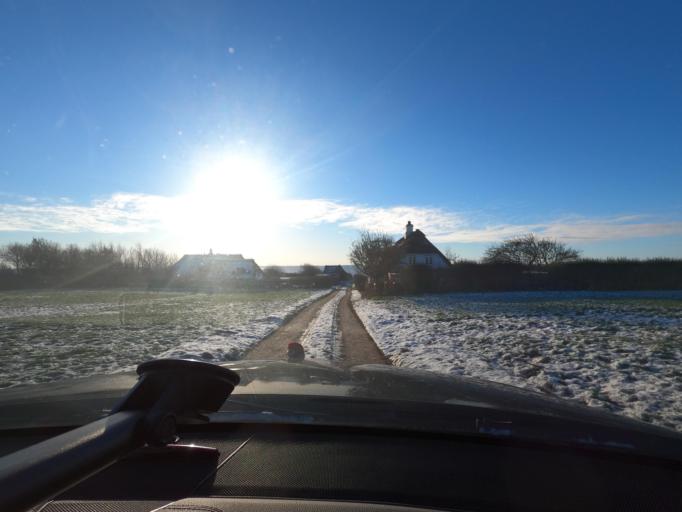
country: DK
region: South Denmark
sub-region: Sonderborg Kommune
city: Horuphav
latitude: 54.8736
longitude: 9.8769
